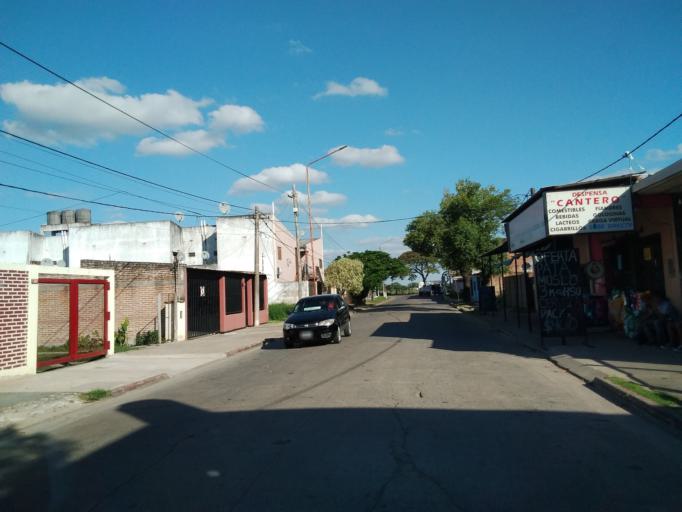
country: AR
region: Corrientes
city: Corrientes
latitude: -27.4619
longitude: -58.7751
